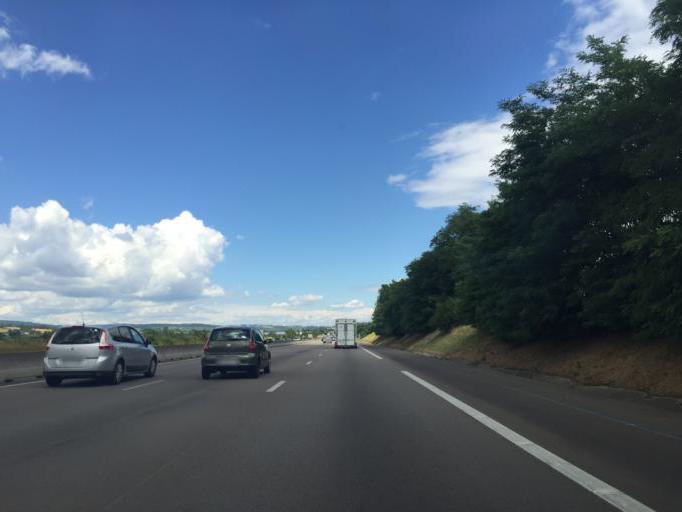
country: FR
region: Rhone-Alpes
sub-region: Departement de l'Isere
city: Auberives-sur-Vareze
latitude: 45.4466
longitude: 4.8280
